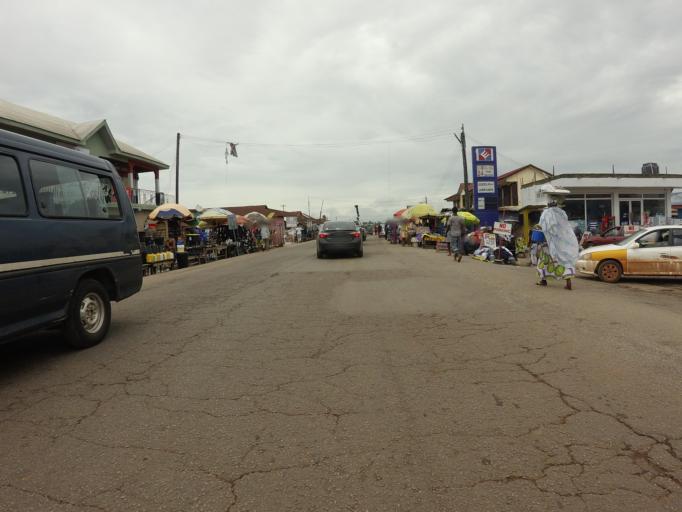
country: GH
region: Eastern
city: Begoro
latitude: 6.3815
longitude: -0.5499
